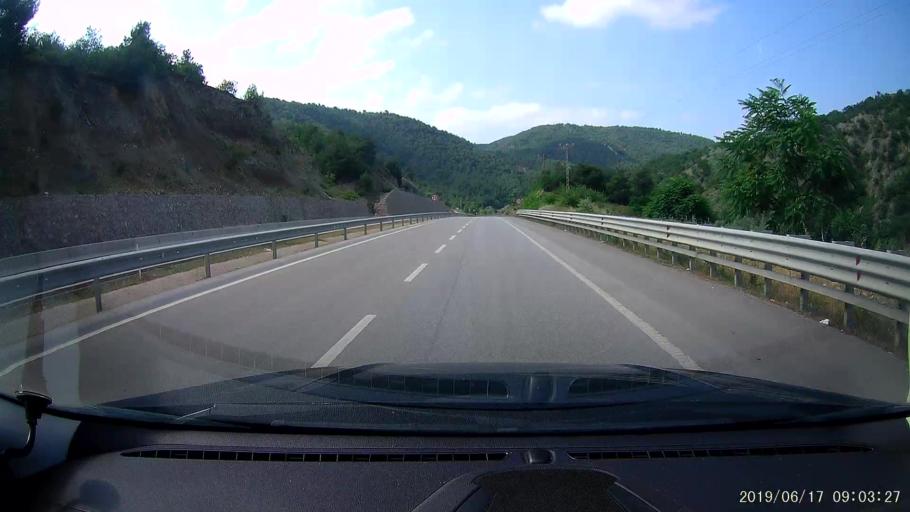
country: TR
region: Amasya
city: Tasova
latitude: 40.7552
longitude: 36.3023
